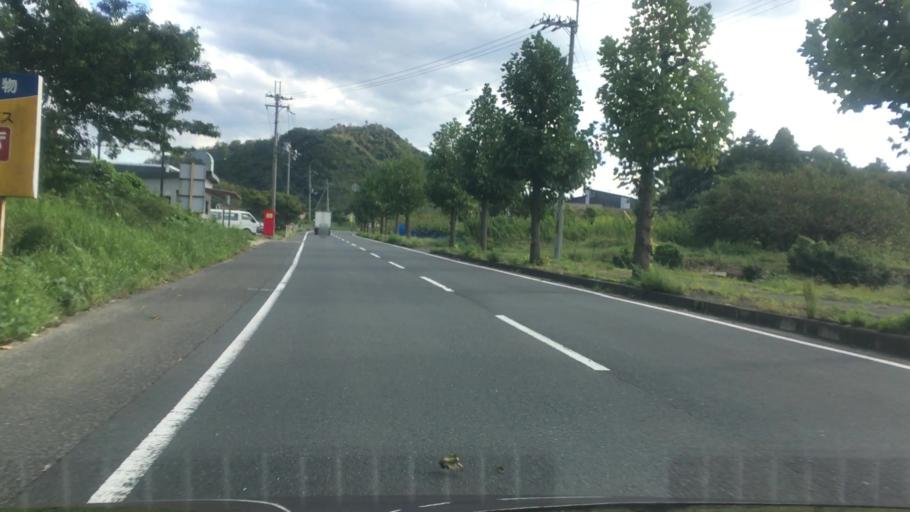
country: JP
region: Hyogo
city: Toyooka
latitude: 35.6247
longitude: 134.9285
